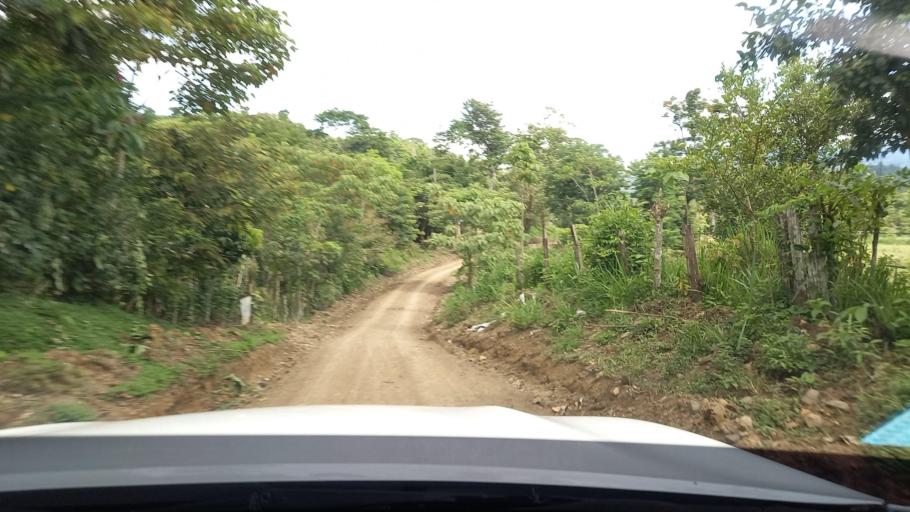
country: NI
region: Jinotega
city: San Jose de Bocay
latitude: 13.3768
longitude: -85.6848
